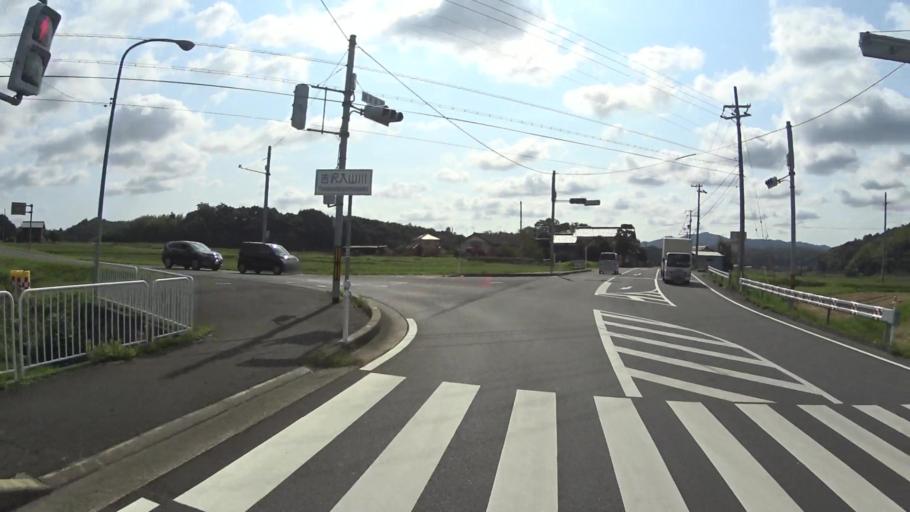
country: JP
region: Kyoto
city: Miyazu
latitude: 35.6428
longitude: 135.0881
